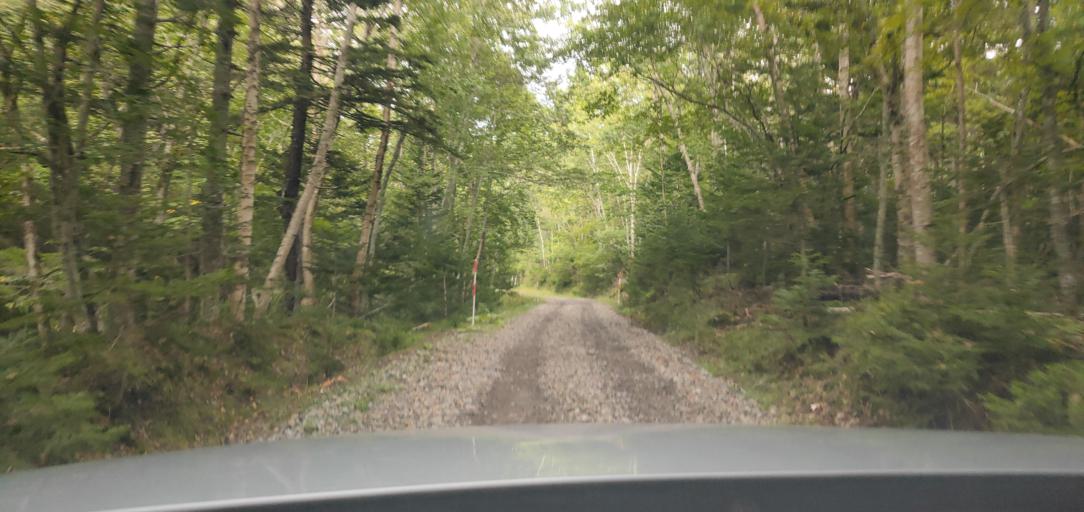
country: JP
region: Hokkaido
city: Kitami
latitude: 43.3700
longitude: 143.9526
